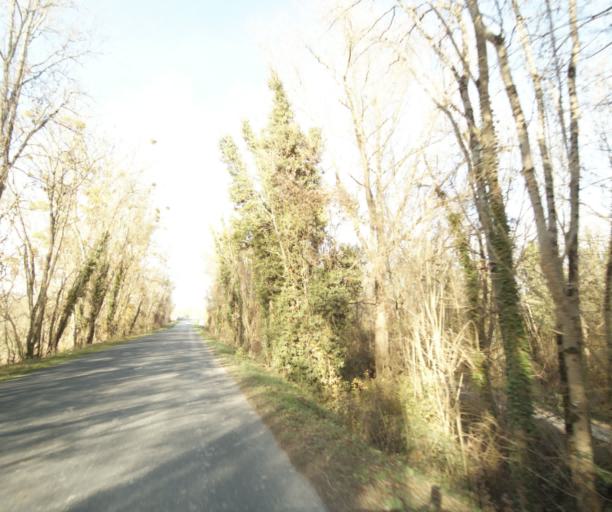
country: FR
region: Poitou-Charentes
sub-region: Departement de la Charente-Maritime
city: Chaniers
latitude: 45.7043
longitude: -0.5288
